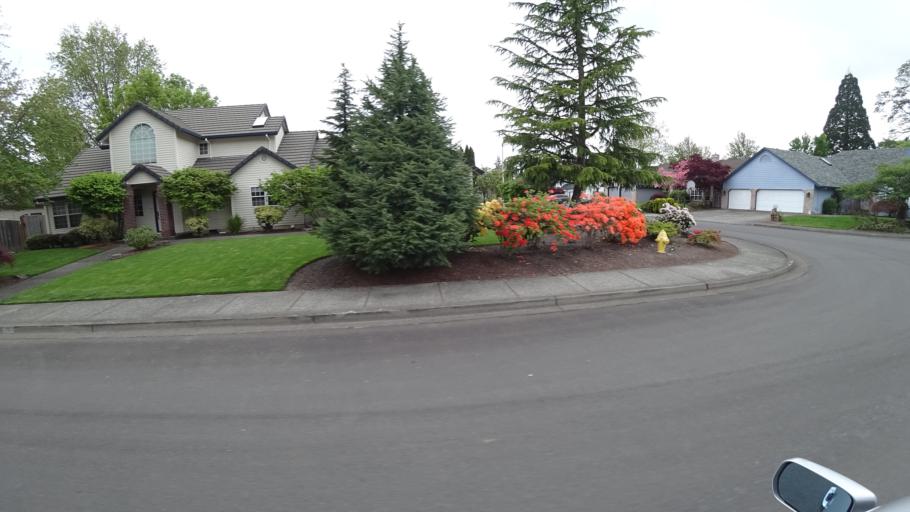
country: US
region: Oregon
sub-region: Washington County
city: Hillsboro
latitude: 45.5370
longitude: -122.9807
